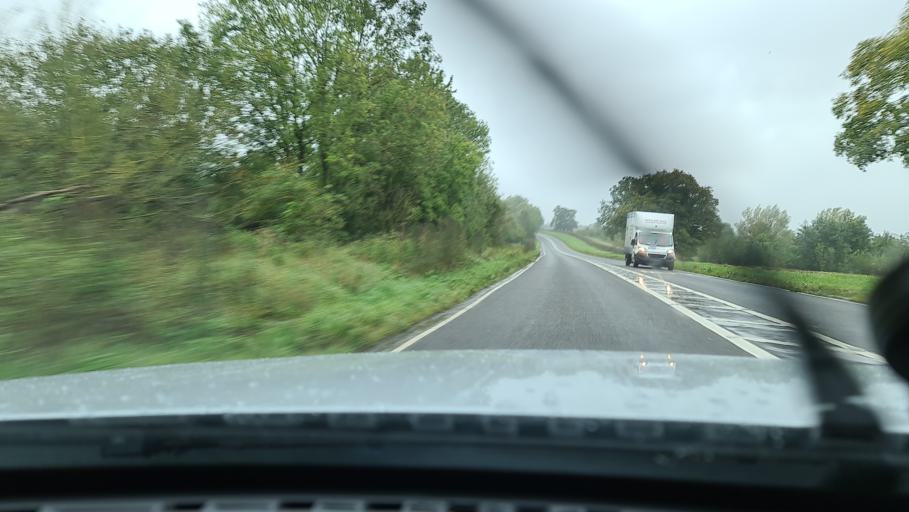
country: GB
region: England
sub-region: Oxfordshire
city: Deddington
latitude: 51.9686
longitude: -1.3202
